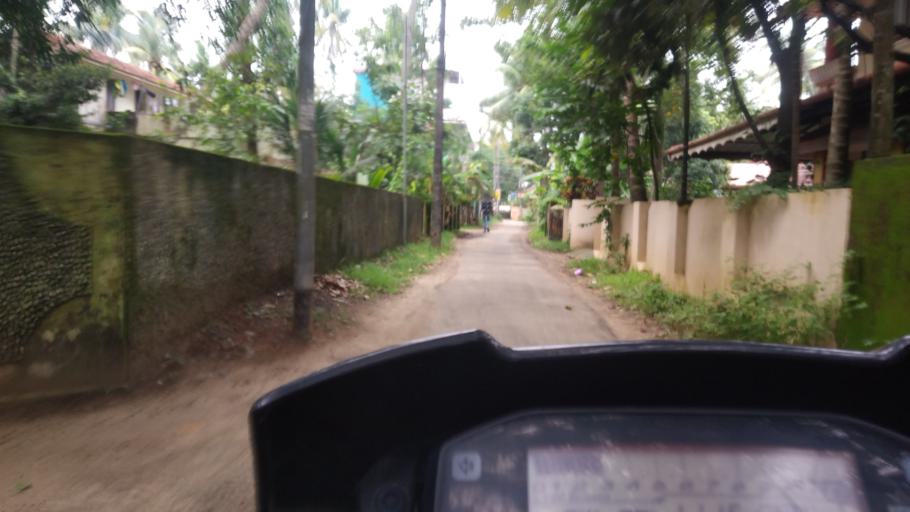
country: IN
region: Kerala
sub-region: Ernakulam
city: Elur
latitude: 10.0611
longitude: 76.2167
